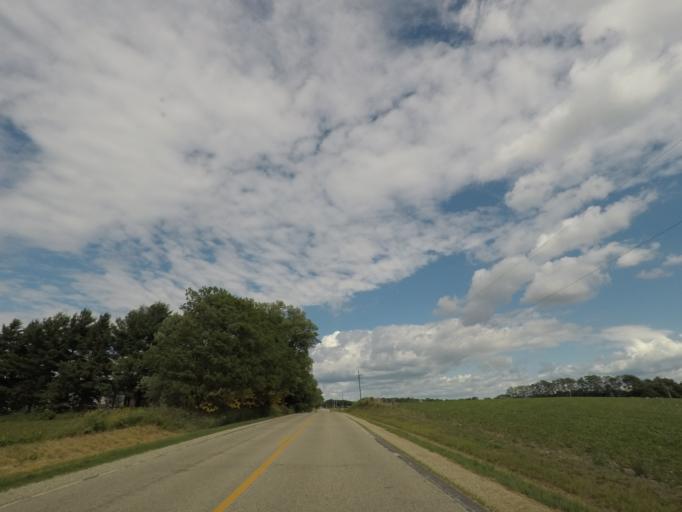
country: US
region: Wisconsin
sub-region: Rock County
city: Orfordville
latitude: 42.7035
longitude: -89.1483
